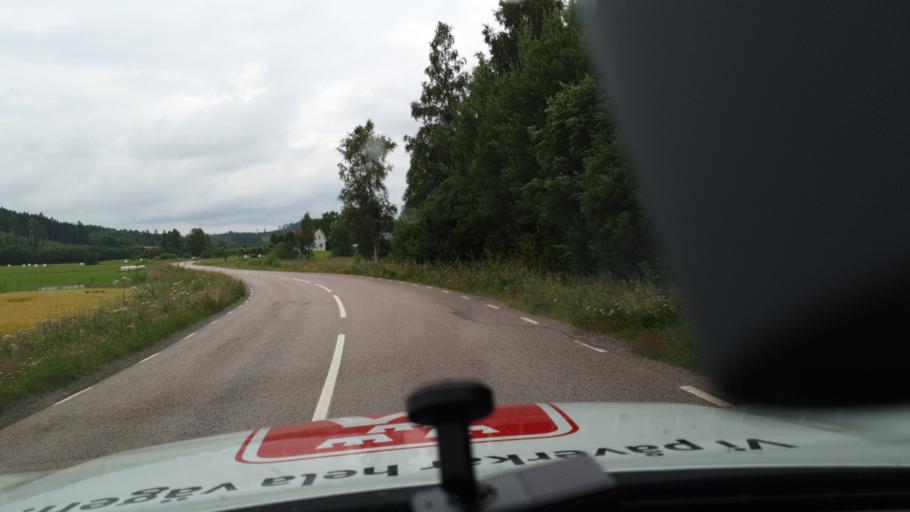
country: SE
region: Vaermland
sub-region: Sunne Kommun
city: Sunne
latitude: 59.7897
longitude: 13.2316
